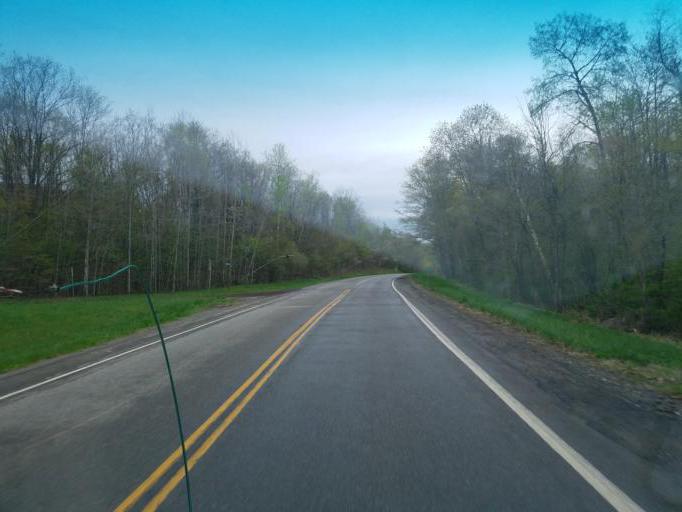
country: US
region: New York
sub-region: Allegany County
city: Wellsville
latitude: 42.0013
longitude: -77.8601
